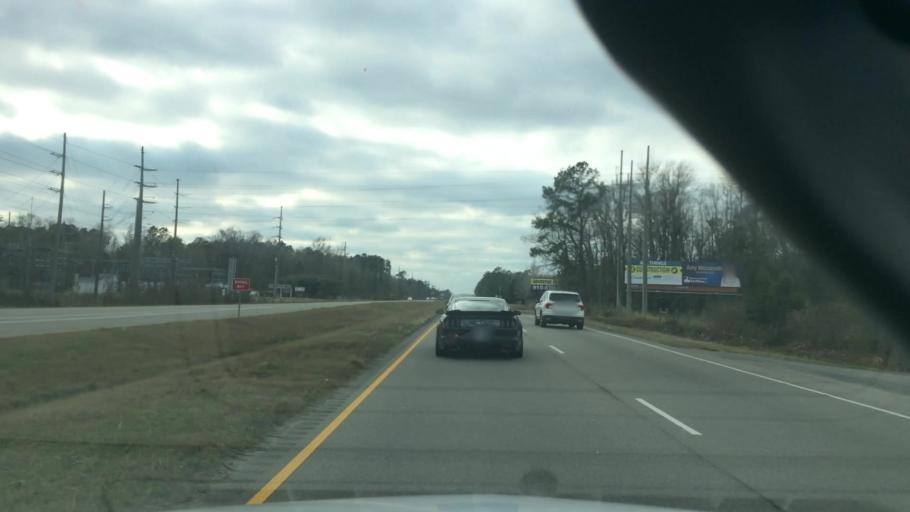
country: US
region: North Carolina
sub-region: Brunswick County
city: Shallotte
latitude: 34.0071
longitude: -78.3023
